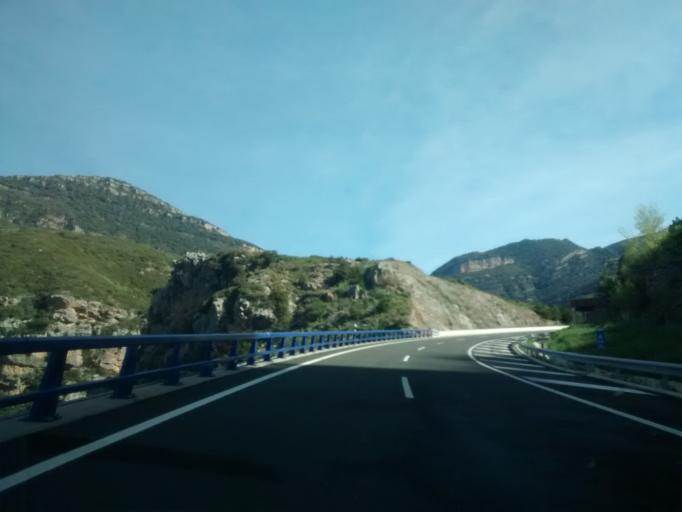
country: ES
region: Aragon
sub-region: Provincia de Huesca
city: Nueno
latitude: 42.2756
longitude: -0.4291
